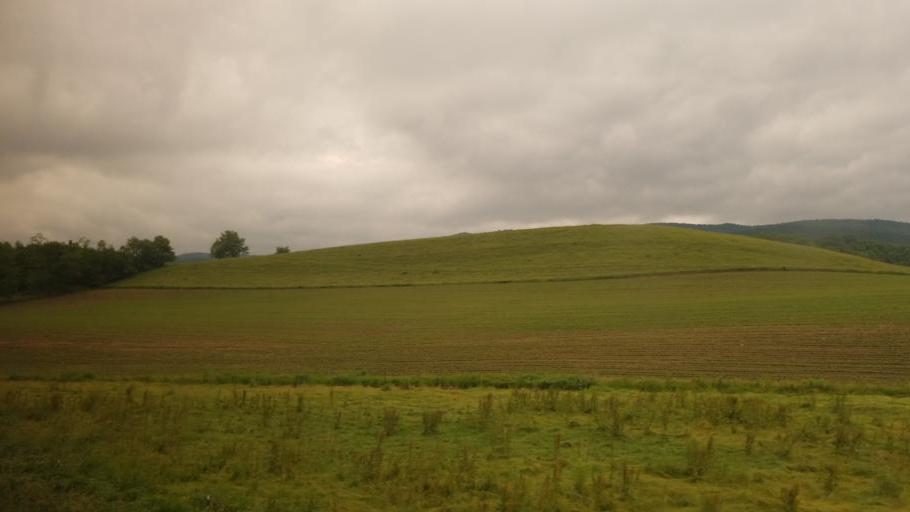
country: US
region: Maryland
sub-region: Allegany County
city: Cumberland
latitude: 39.7462
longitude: -78.7426
